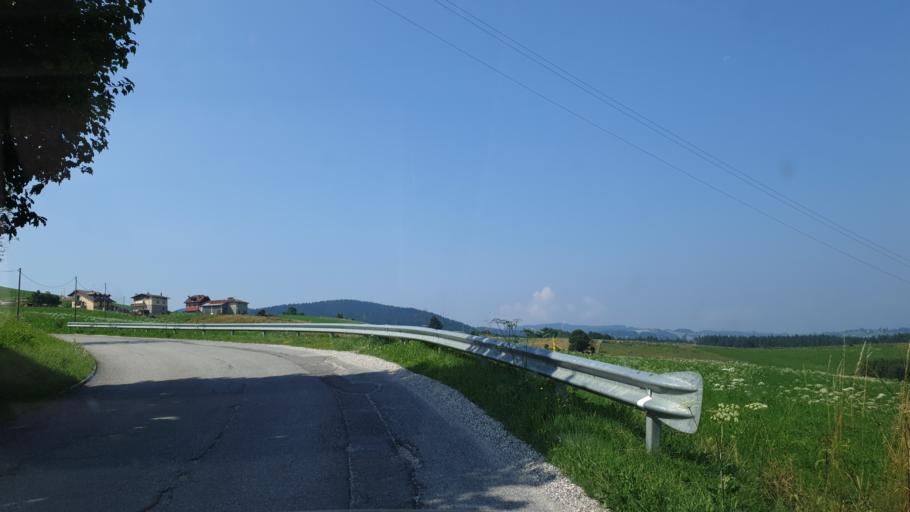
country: IT
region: Veneto
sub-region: Provincia di Vicenza
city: Canove di Roana
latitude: 45.8535
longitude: 11.4950
